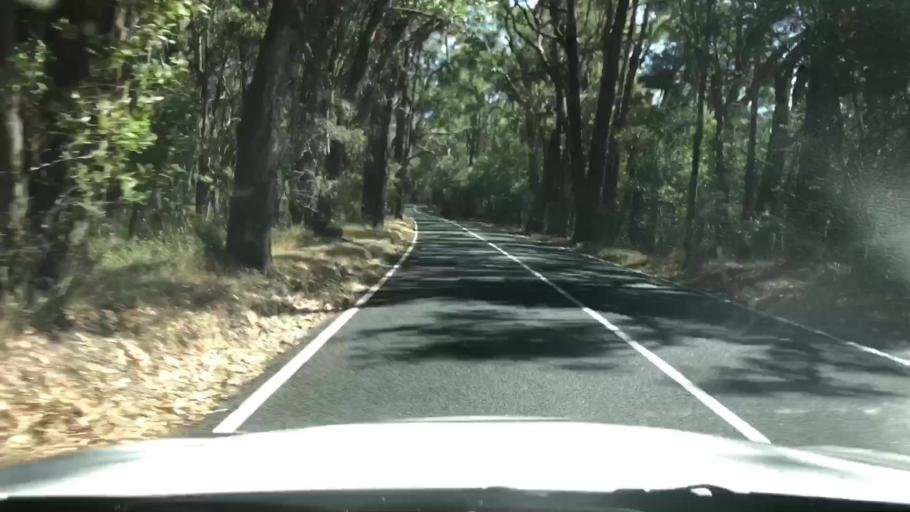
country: AU
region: Victoria
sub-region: Yarra Ranges
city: Macclesfield
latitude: -37.8522
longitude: 145.4856
